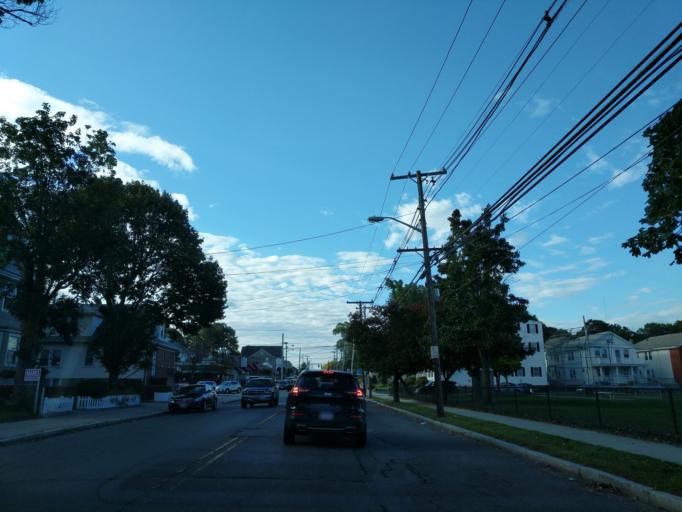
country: US
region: Massachusetts
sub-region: Middlesex County
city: Malden
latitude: 42.4109
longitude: -71.0795
